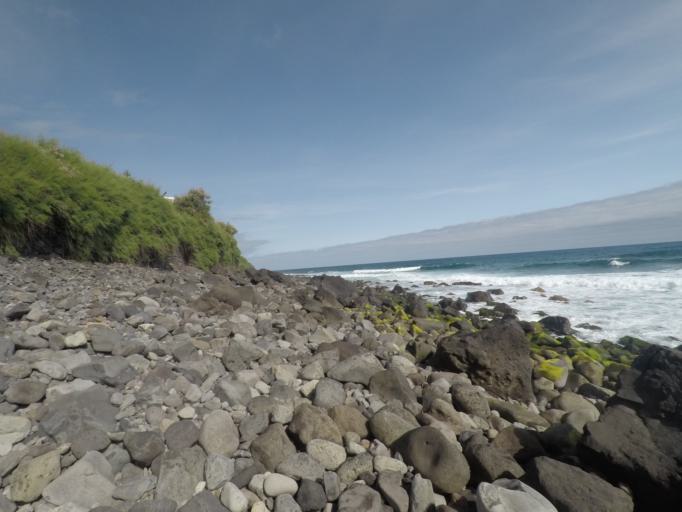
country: PT
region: Madeira
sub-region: Sao Vicente
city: Sao Vicente
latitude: 32.8293
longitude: -16.9856
